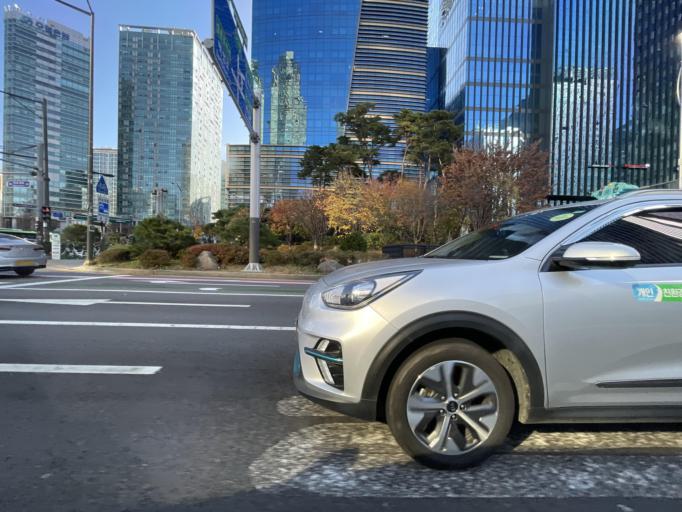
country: KR
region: Seoul
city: Seoul
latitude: 37.5436
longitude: 126.9509
